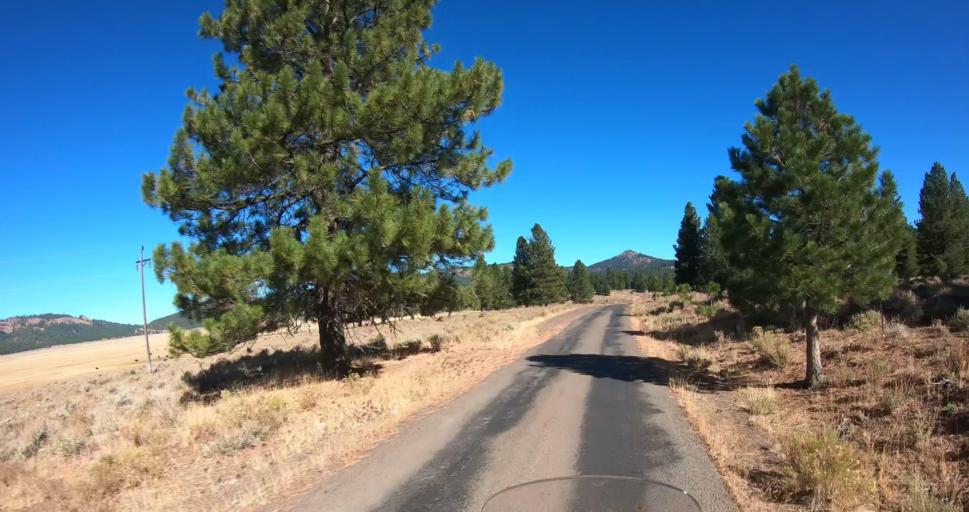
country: US
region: Oregon
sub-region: Lake County
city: Lakeview
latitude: 42.2091
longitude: -120.2549
